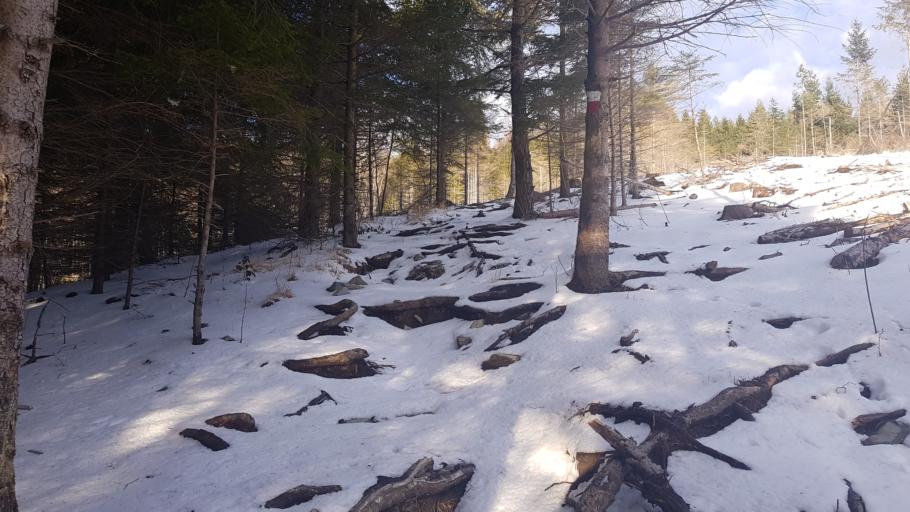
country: IT
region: Friuli Venezia Giulia
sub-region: Provincia di Udine
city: Torreano
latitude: 46.1806
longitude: 13.4089
